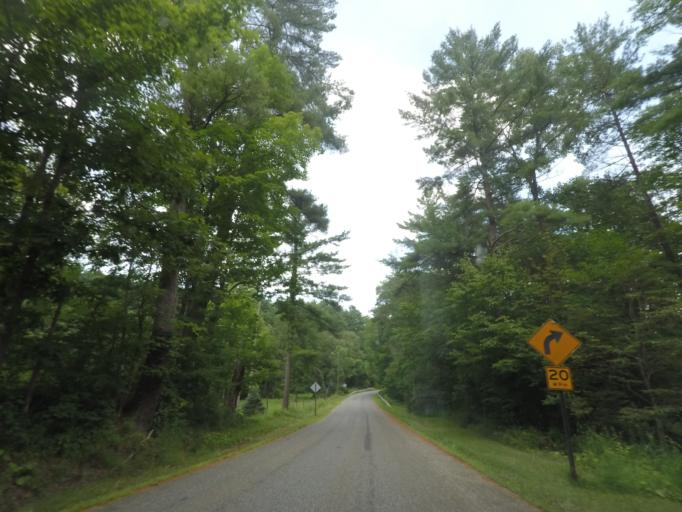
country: US
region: New York
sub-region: Saratoga County
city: Stillwater
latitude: 43.0088
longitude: -73.6222
